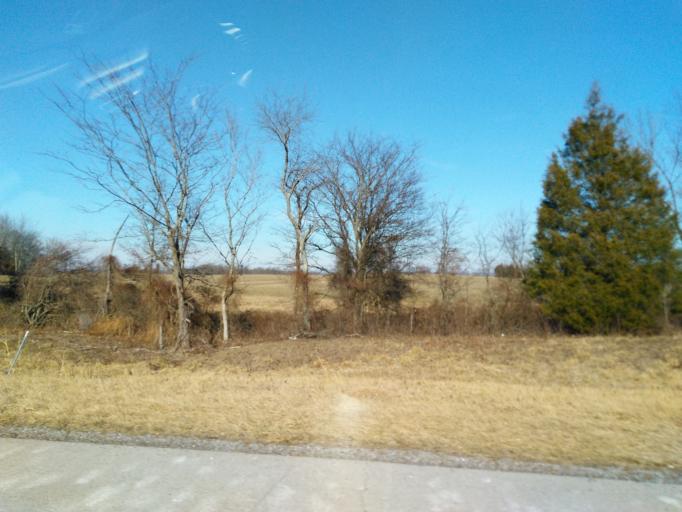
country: US
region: Illinois
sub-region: Johnson County
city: Vienna
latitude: 37.3879
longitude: -88.8324
